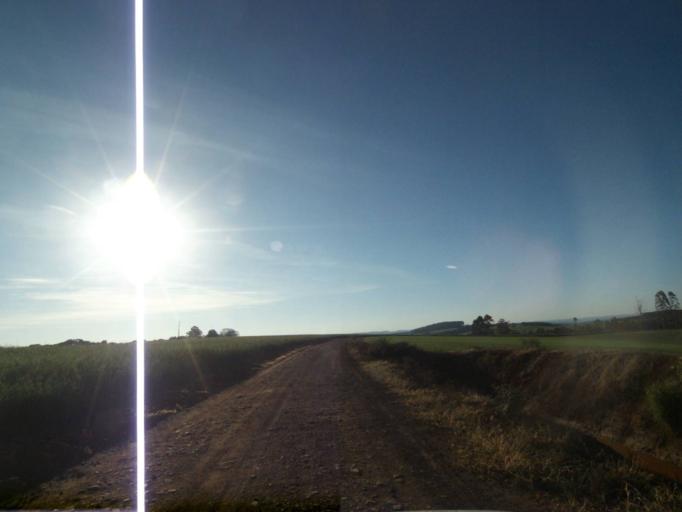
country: BR
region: Parana
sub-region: Telemaco Borba
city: Telemaco Borba
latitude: -24.4847
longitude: -50.5935
